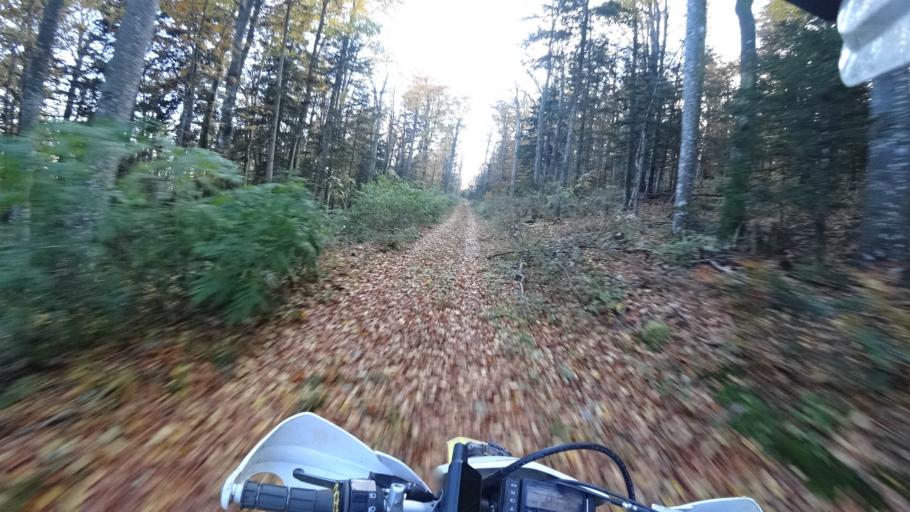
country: HR
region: Karlovacka
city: Plaski
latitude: 44.9544
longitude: 15.4067
